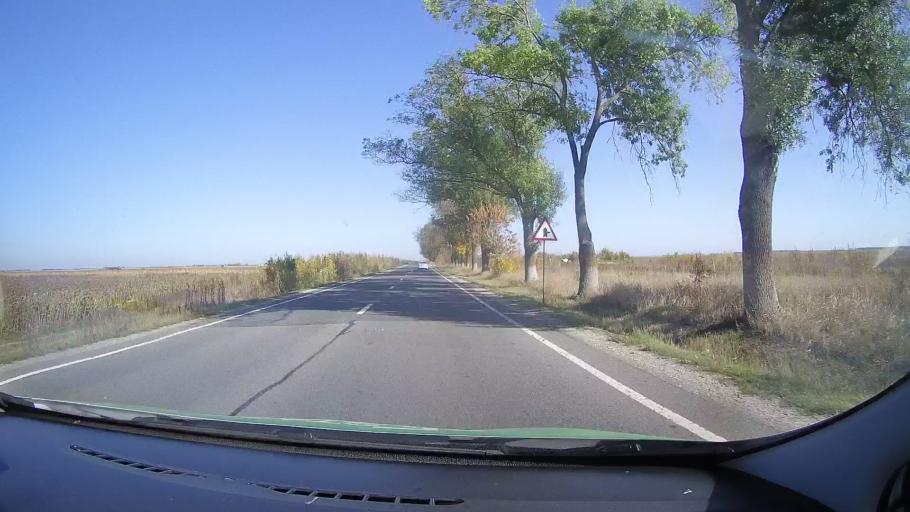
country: RO
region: Satu Mare
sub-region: Comuna Moftinu
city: Moftinu Mic
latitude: 47.7107
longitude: 22.6428
